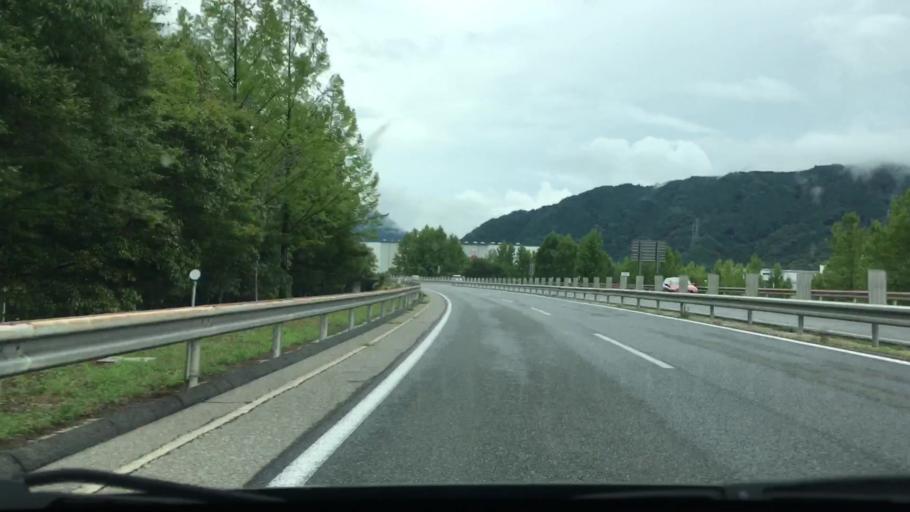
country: JP
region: Hiroshima
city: Hiroshima-shi
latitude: 34.5753
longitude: 132.4579
